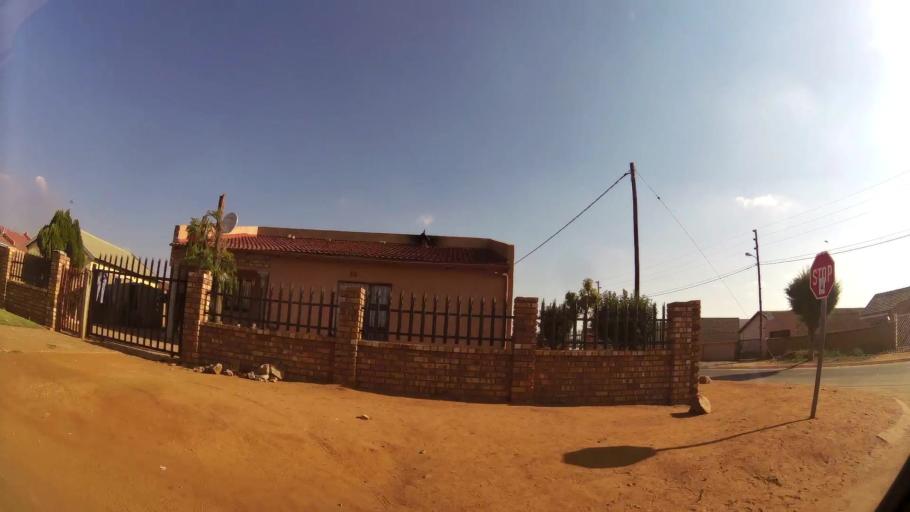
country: ZA
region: Gauteng
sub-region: Ekurhuleni Metropolitan Municipality
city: Benoni
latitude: -26.2273
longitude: 28.3243
